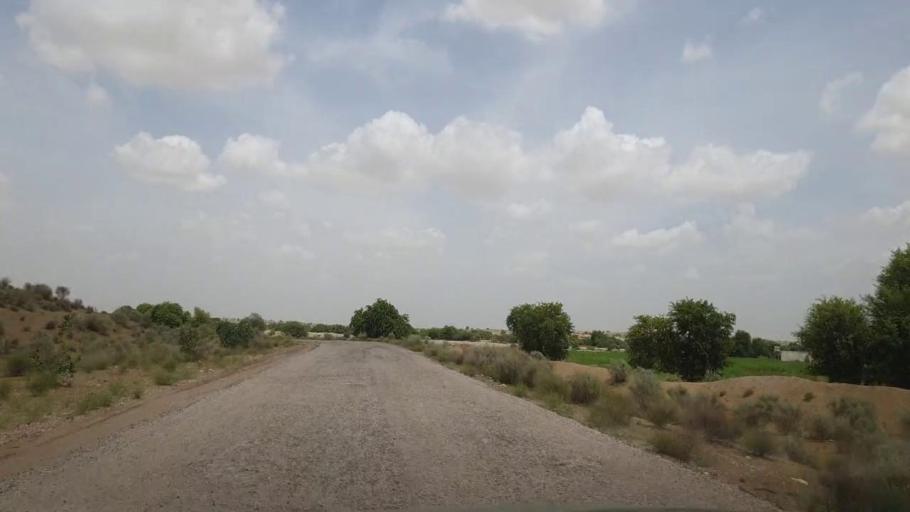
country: PK
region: Sindh
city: Kot Diji
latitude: 27.2008
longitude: 69.1267
